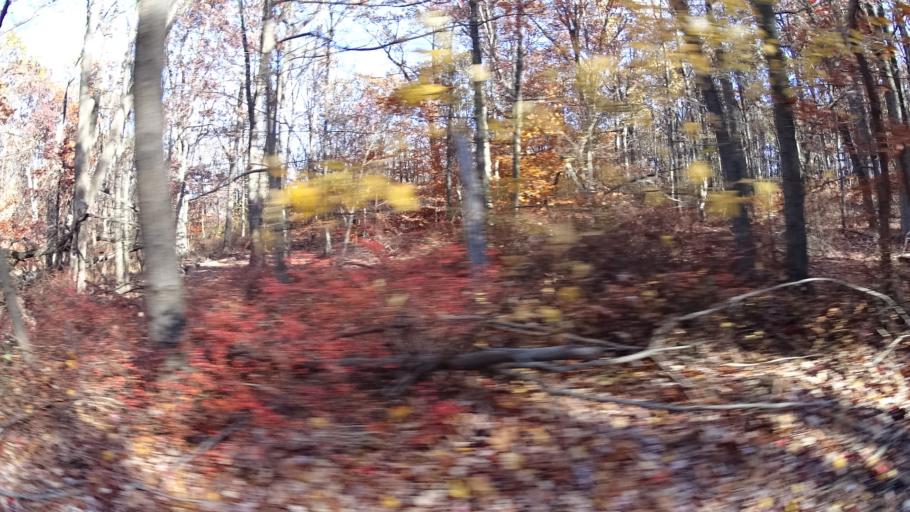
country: US
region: New Jersey
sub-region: Union County
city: Scotch Plains
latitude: 40.6672
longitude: -74.3939
